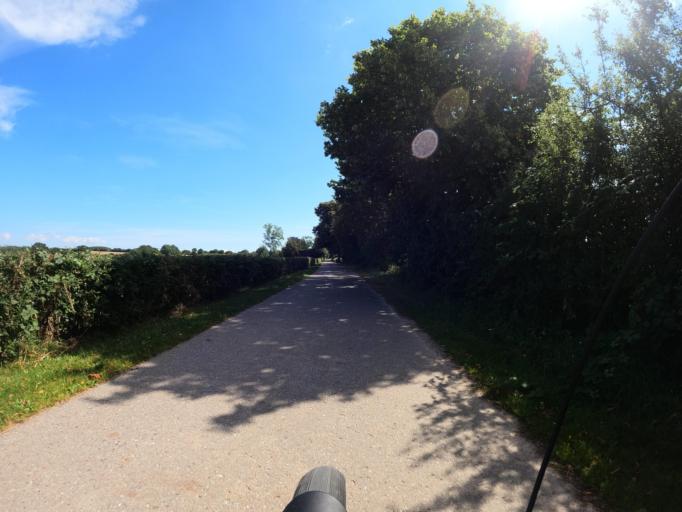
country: DE
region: Schleswig-Holstein
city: Dollerup
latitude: 54.7779
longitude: 9.6869
